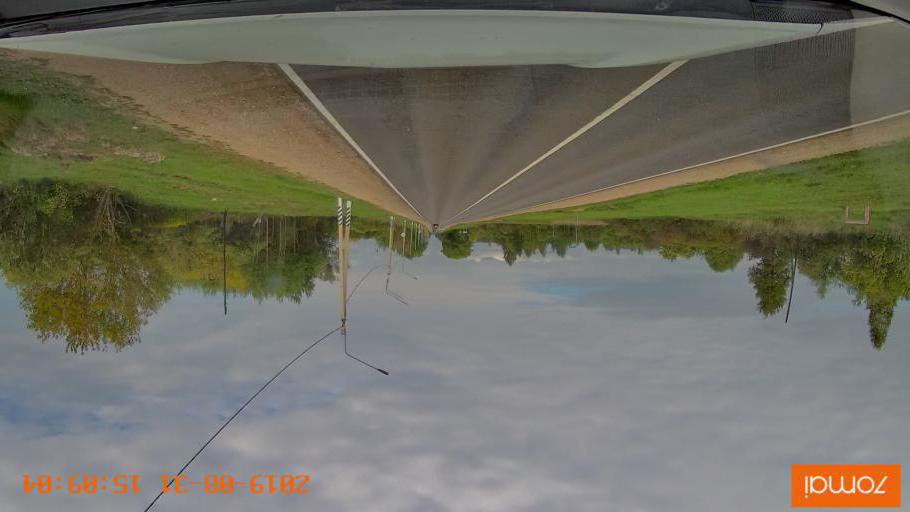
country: RU
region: Kaluga
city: Spas-Demensk
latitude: 54.3978
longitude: 34.1939
